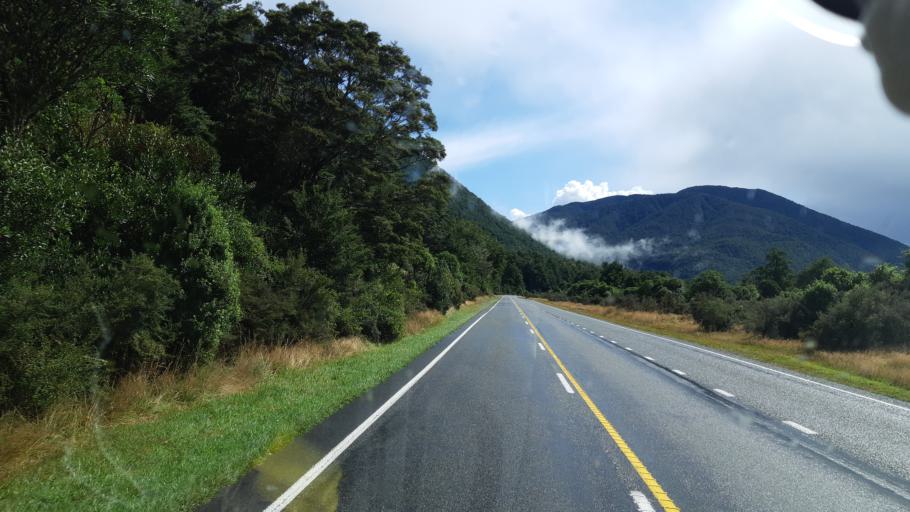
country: NZ
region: Canterbury
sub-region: Hurunui District
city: Amberley
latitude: -42.3814
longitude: 172.2897
